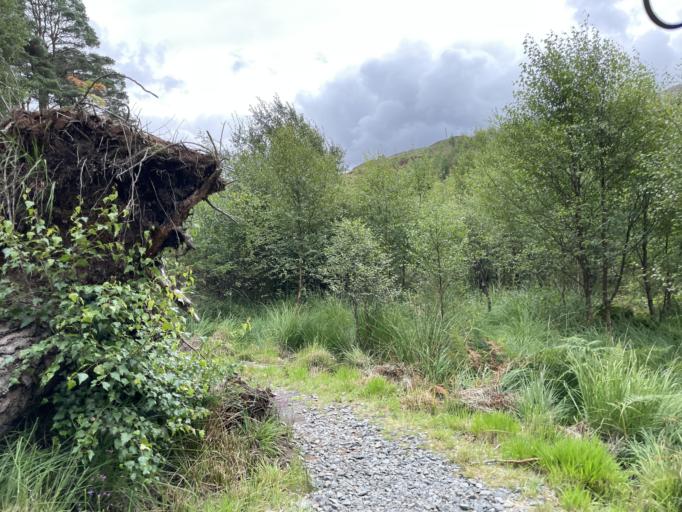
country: GB
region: Scotland
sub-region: Dumfries and Galloway
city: Newton Stewart
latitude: 55.0833
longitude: -4.4975
